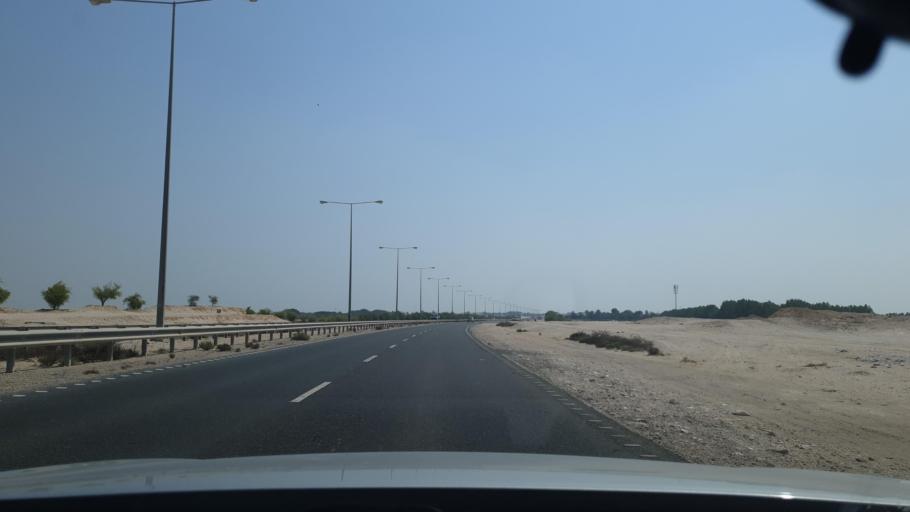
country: QA
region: Al Khawr
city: Al Khawr
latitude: 25.7354
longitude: 51.4920
